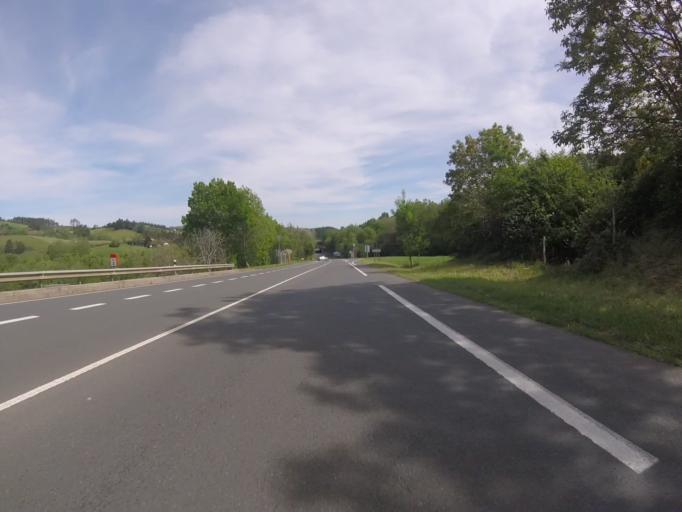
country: ES
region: Basque Country
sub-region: Provincia de Guipuzcoa
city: Cestona
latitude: 43.2627
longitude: -2.2715
